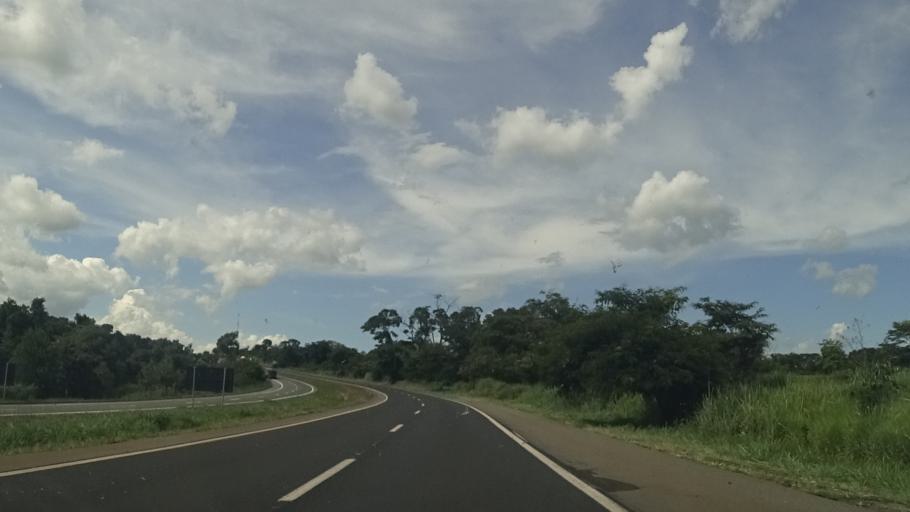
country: BR
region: Goias
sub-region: Piracanjuba
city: Piracanjuba
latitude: -17.3001
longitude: -49.2343
